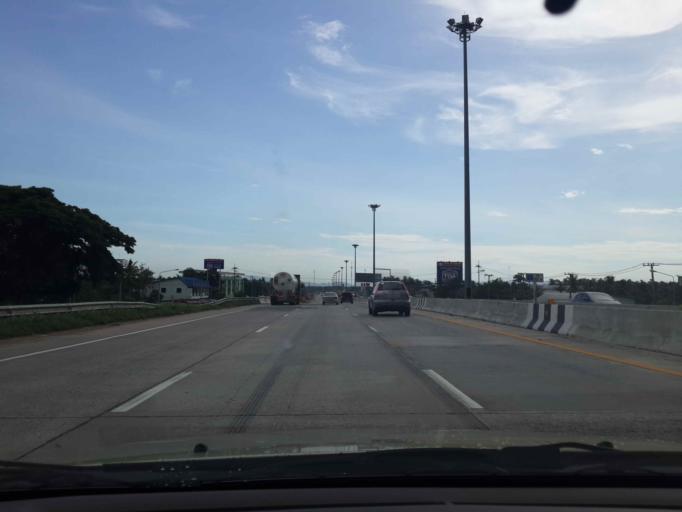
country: TH
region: Chon Buri
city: Ban Talat Bueng
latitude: 13.0007
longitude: 100.9926
